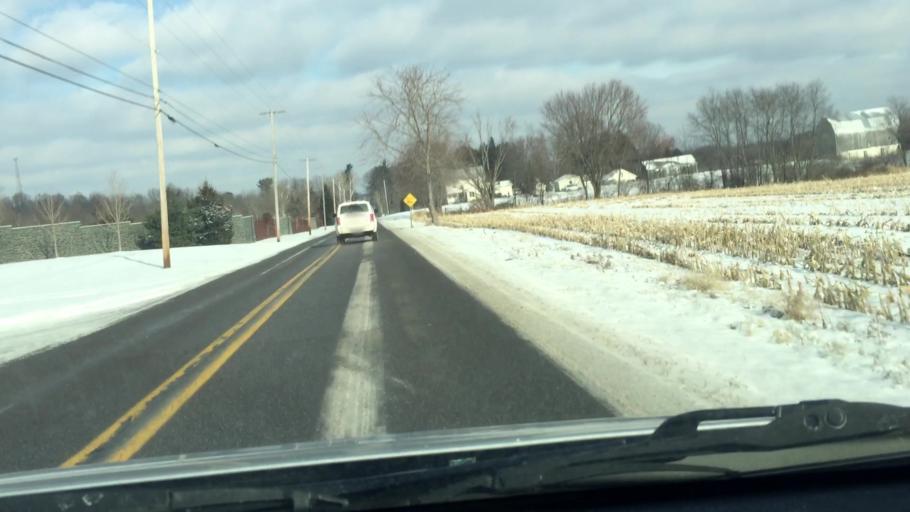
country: US
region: Ohio
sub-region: Mahoning County
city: Boardman
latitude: 41.0085
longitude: -80.7113
